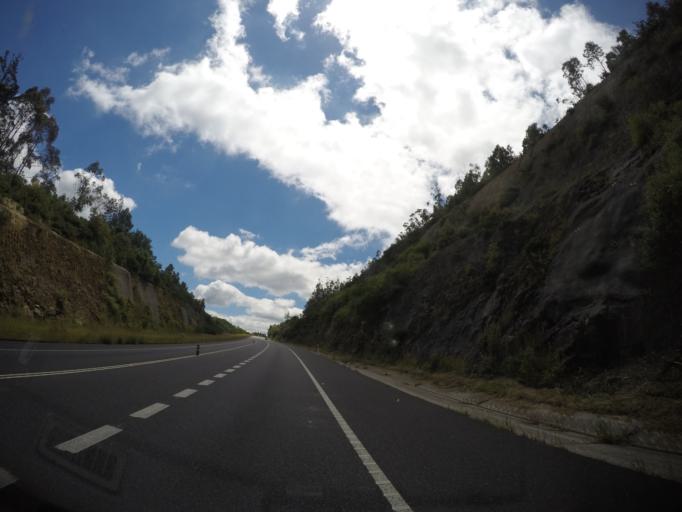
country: ES
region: Aragon
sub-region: Provincia de Zaragoza
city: El Burgo de Ebro
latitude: 41.5484
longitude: -0.7474
